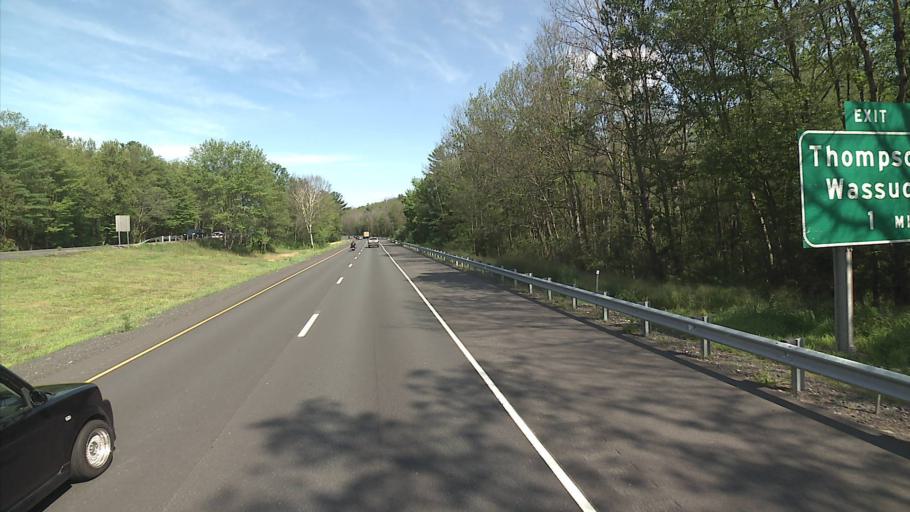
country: US
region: Connecticut
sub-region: Hartford County
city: Terramuggus
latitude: 41.6551
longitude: -72.5023
